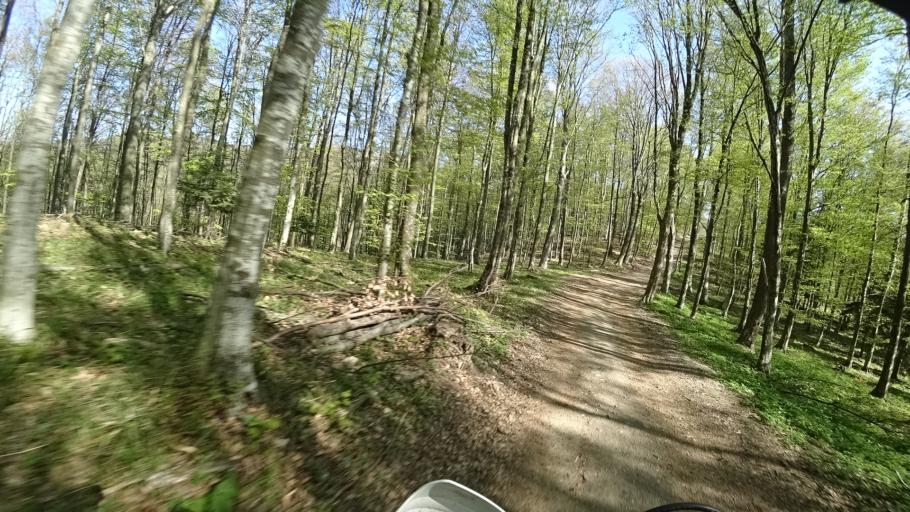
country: HR
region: Zagrebacka
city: Jablanovec
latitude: 45.8951
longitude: 15.9180
